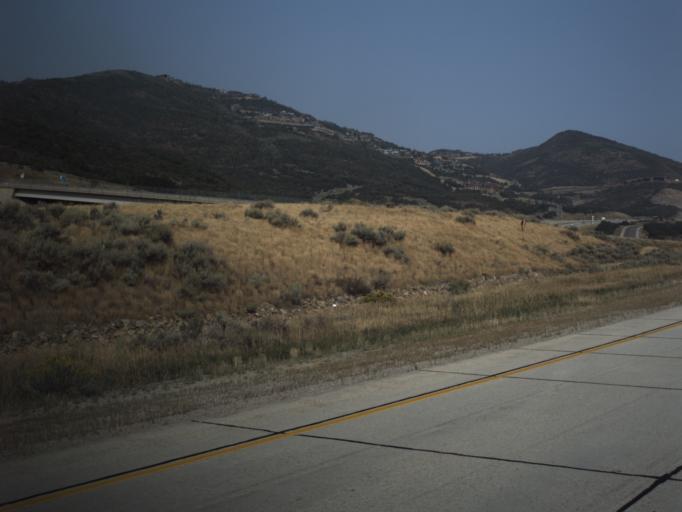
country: US
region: Utah
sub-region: Summit County
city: Park City
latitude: 40.6245
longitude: -111.4388
